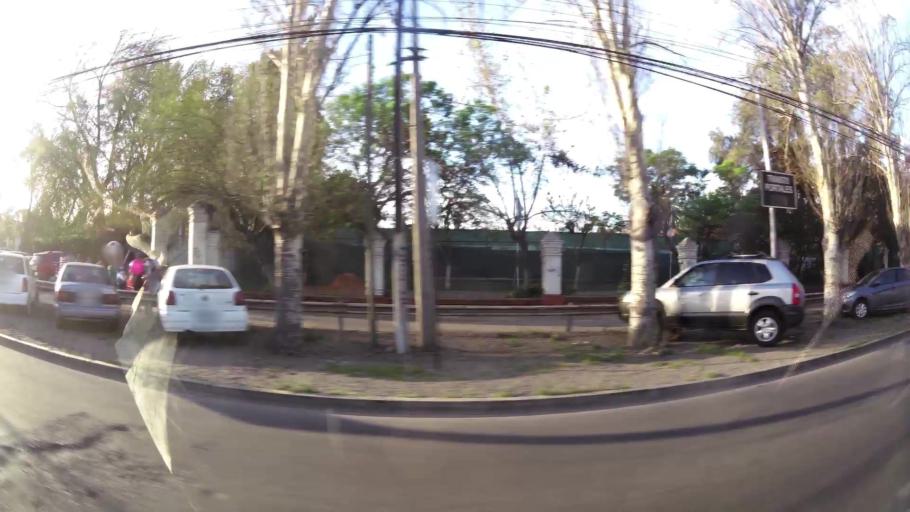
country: CL
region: Santiago Metropolitan
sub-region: Provincia de Santiago
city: Santiago
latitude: -33.4440
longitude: -70.6836
